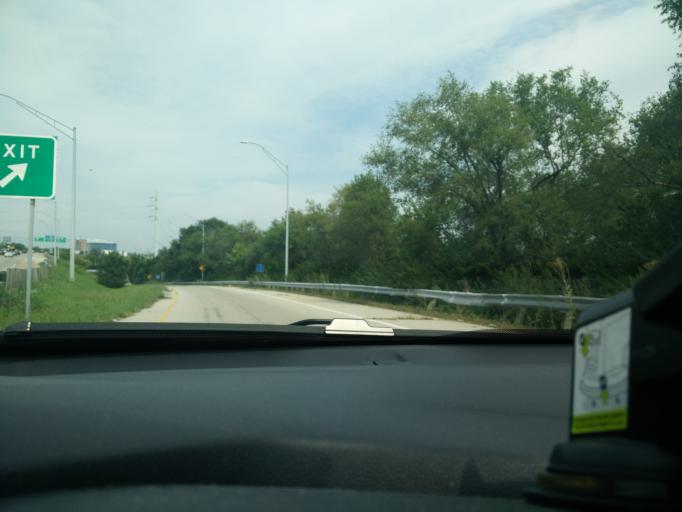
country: US
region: Ohio
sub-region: Montgomery County
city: Dayton
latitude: 39.7706
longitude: -84.1821
